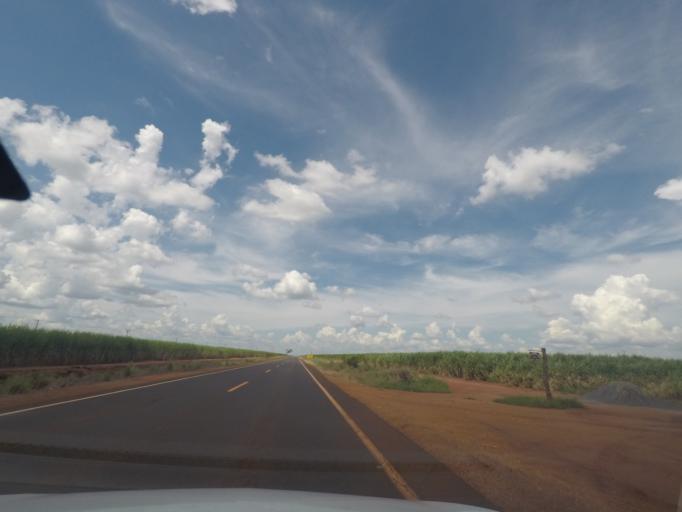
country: BR
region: Minas Gerais
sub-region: Conceicao Das Alagoas
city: Conceicao das Alagoas
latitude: -19.8666
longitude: -48.6124
